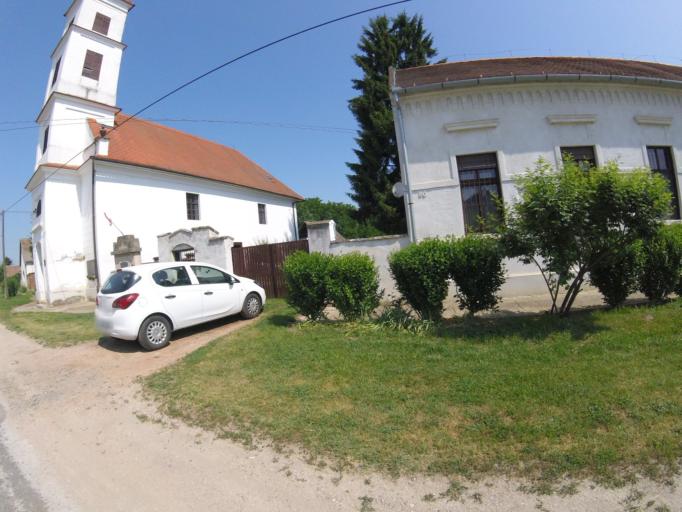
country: HU
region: Baranya
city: Harkany
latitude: 45.8322
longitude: 18.1873
